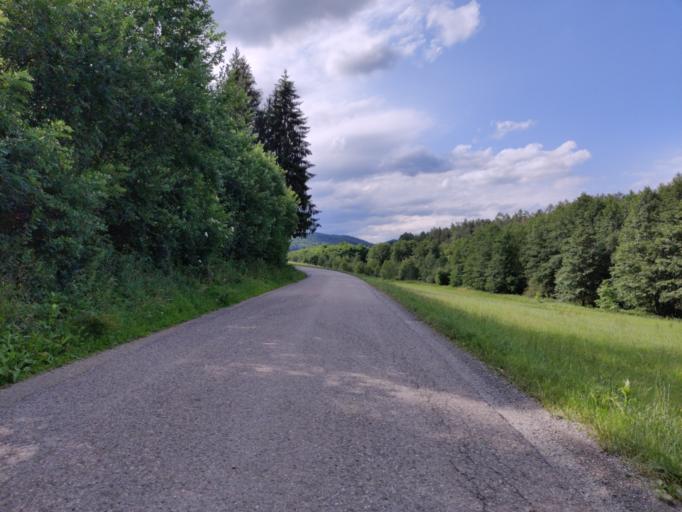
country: AT
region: Styria
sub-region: Politischer Bezirk Graz-Umgebung
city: Thal
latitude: 47.0629
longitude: 15.3448
